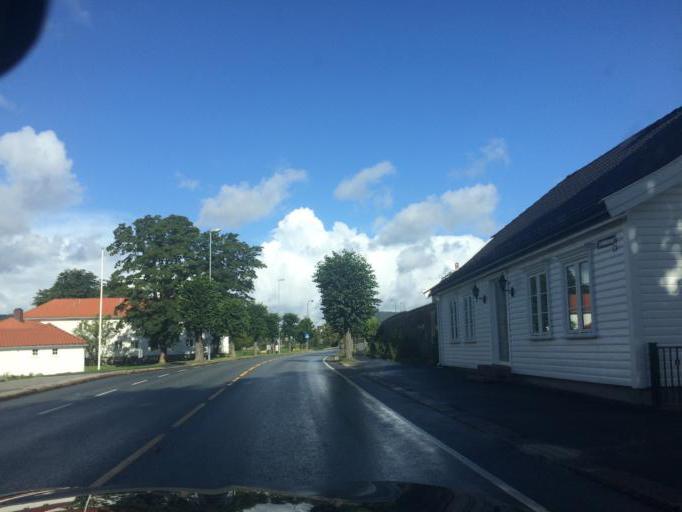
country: NO
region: Vest-Agder
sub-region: Kristiansand
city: Kristiansand
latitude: 58.1533
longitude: 8.0056
